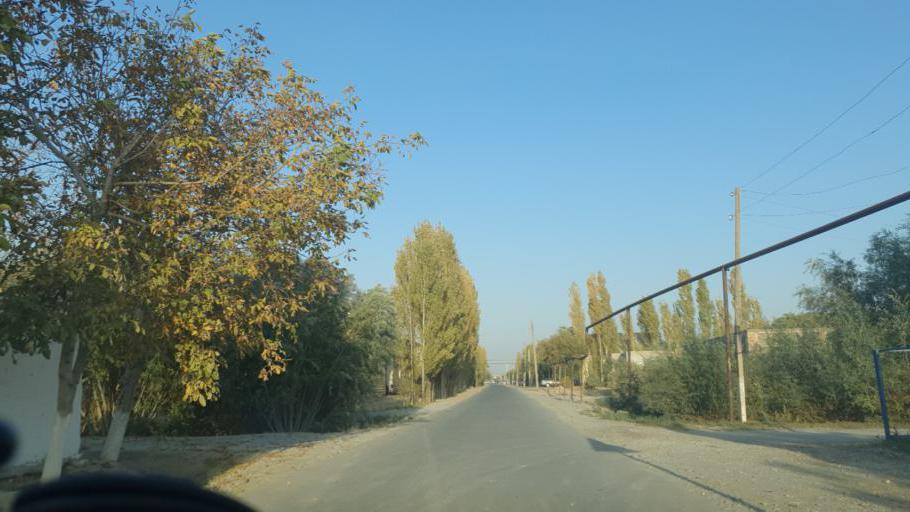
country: UZ
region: Fergana
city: Beshariq
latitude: 40.4651
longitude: 70.5537
